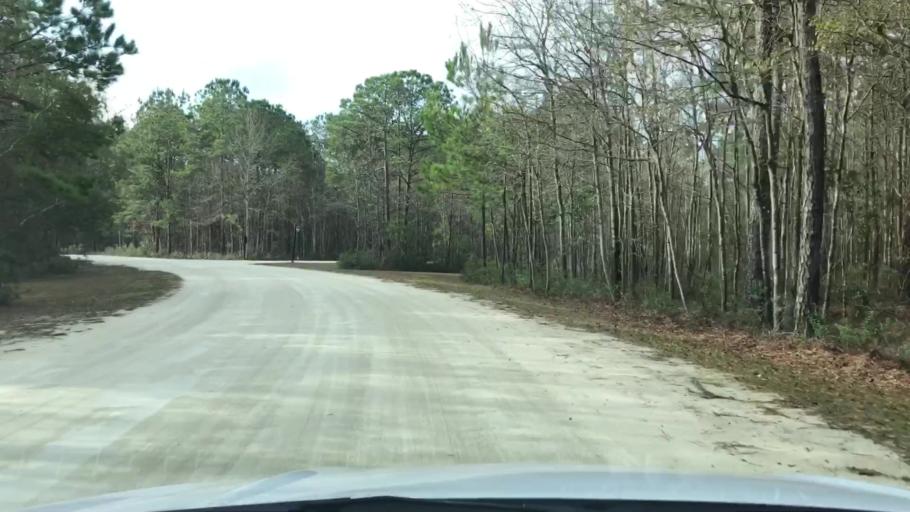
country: US
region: South Carolina
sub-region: Charleston County
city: Isle of Palms
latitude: 32.9018
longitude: -79.7260
